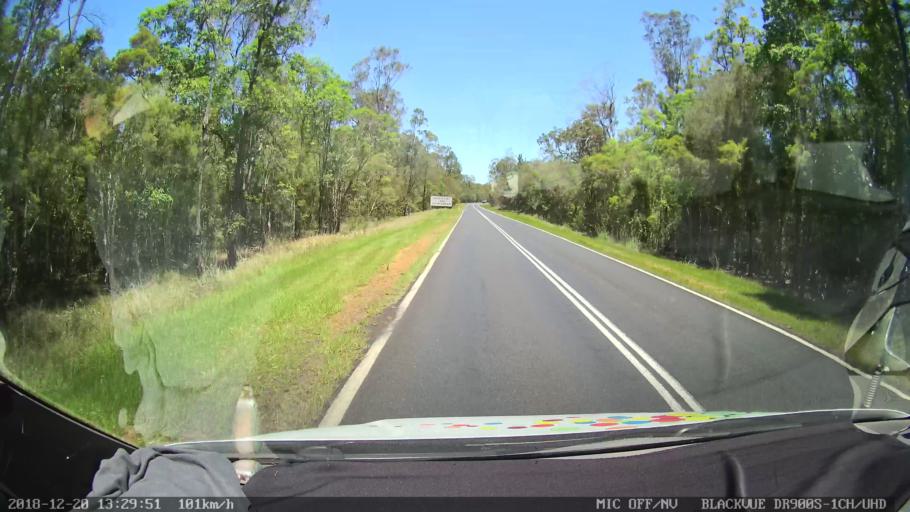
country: AU
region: New South Wales
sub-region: Clarence Valley
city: Gordon
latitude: -29.1952
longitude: 152.9913
